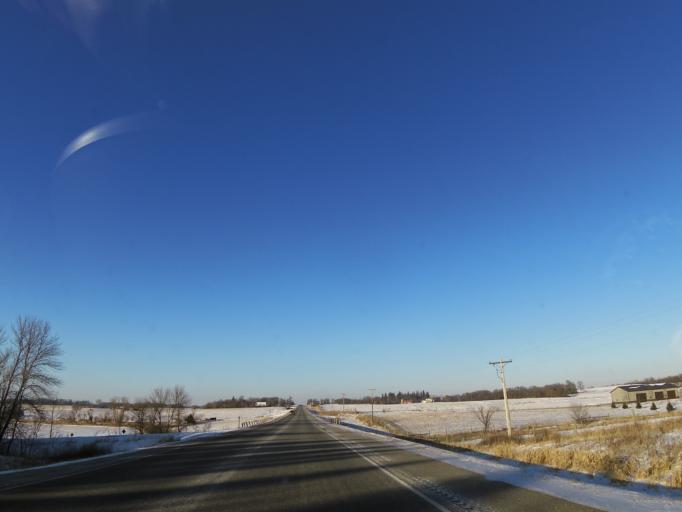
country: US
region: Minnesota
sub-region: Rice County
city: Lonsdale
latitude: 44.5072
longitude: -93.4429
